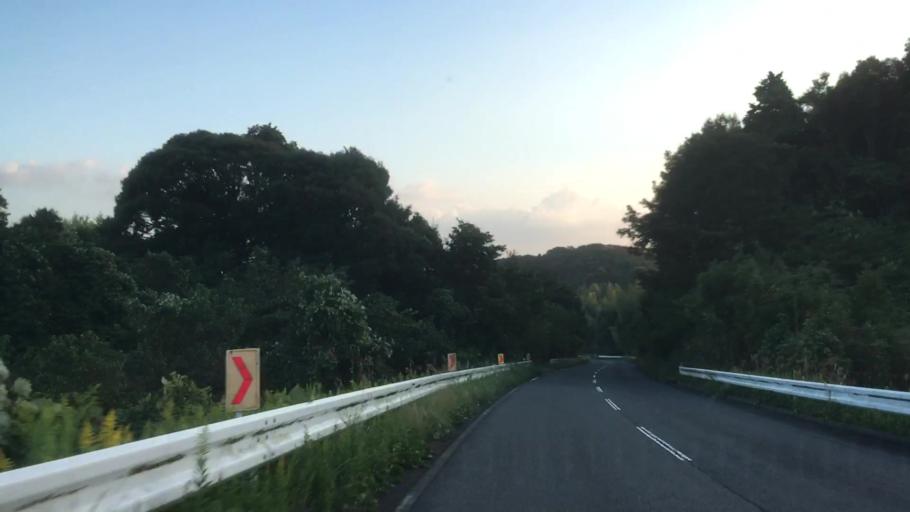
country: JP
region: Nagasaki
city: Sasebo
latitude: 33.0132
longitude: 129.7068
